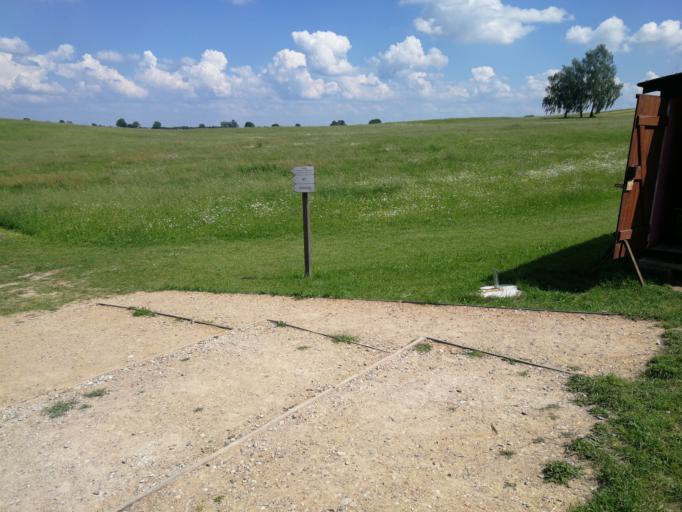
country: PL
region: Warmian-Masurian Voivodeship
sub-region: Powiat ostrodzki
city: Gierzwald
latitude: 53.4885
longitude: 20.1198
